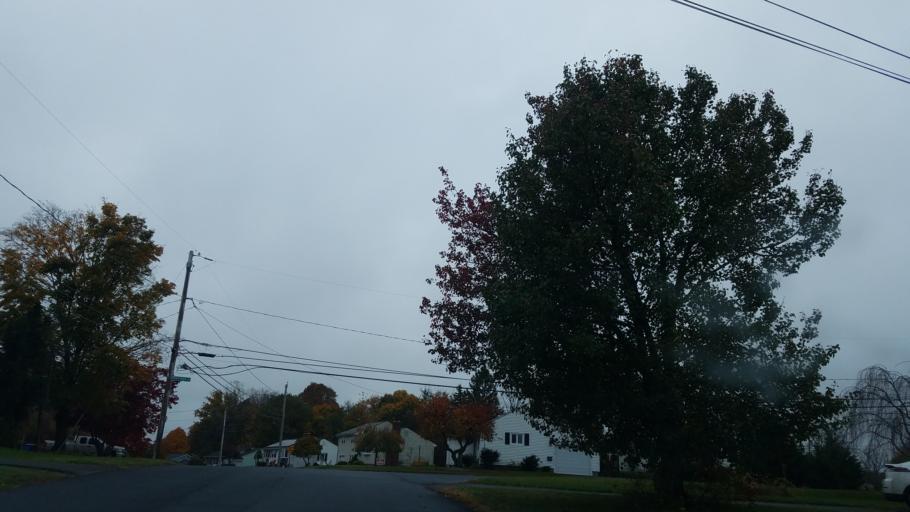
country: US
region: Connecticut
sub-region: Hartford County
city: New Britain
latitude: 41.7130
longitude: -72.7795
